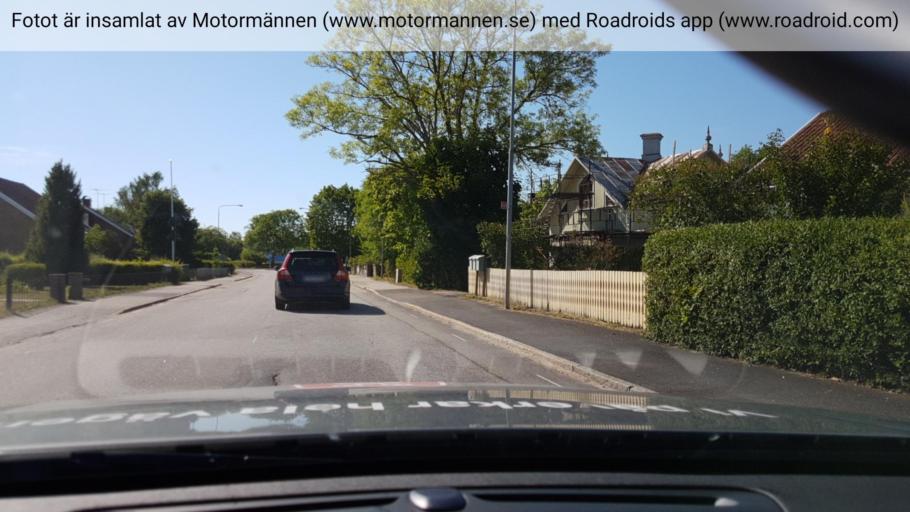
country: SE
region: Vaestra Goetaland
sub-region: Toreboda Kommun
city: Toereboda
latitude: 58.7101
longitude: 14.1380
